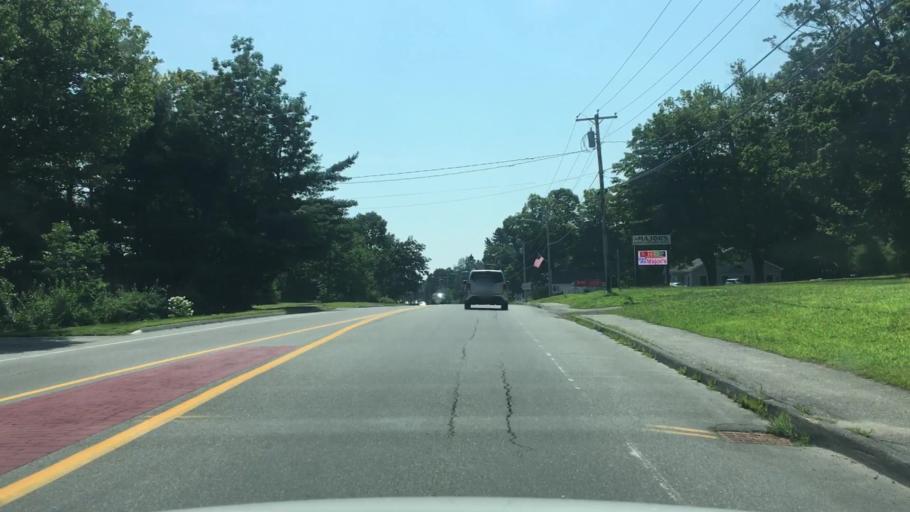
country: US
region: Maine
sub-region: Kennebec County
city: Hallowell
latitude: 44.2649
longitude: -69.7840
